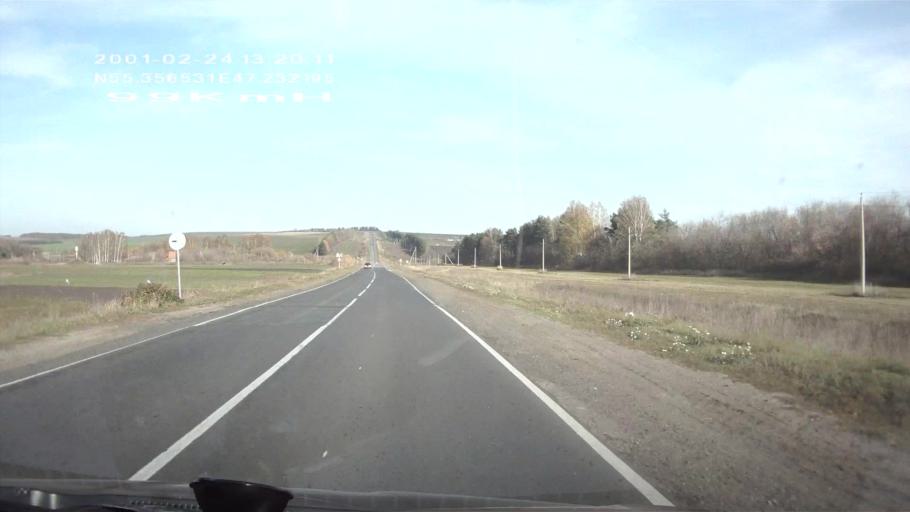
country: RU
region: Chuvashia
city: Ibresi
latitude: 55.3566
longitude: 47.2323
